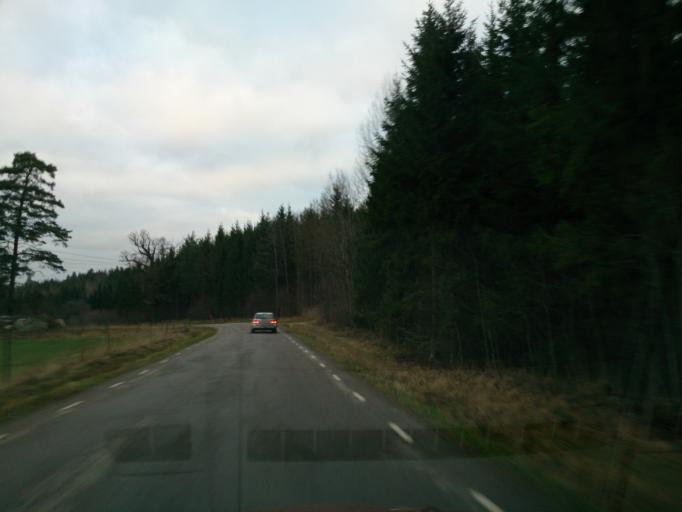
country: SE
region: OEstergoetland
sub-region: Atvidabergs Kommun
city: Atvidaberg
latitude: 58.3313
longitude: 16.0372
